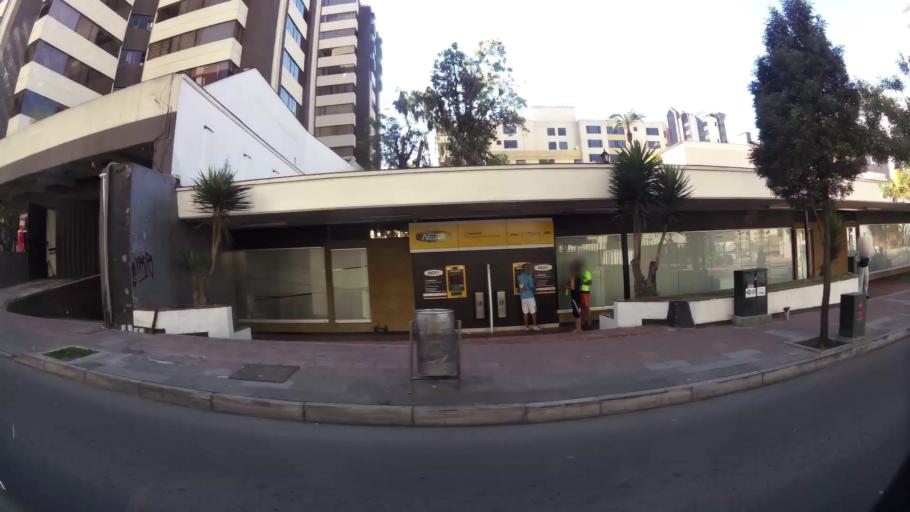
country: EC
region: Pichincha
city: Quito
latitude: -0.1816
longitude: -78.4786
